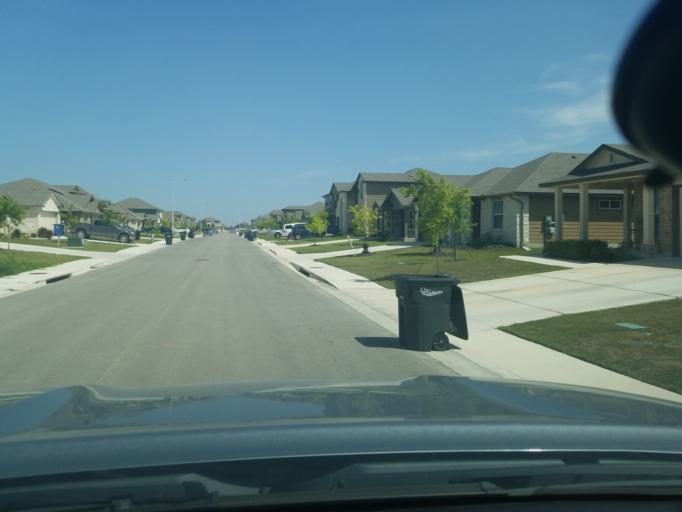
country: US
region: Texas
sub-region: Guadalupe County
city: Lake Dunlap
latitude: 29.6755
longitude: -98.0346
